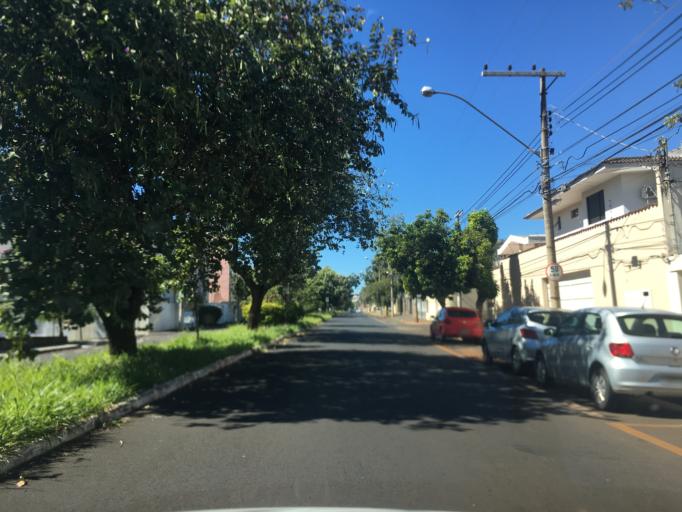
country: BR
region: Minas Gerais
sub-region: Uberlandia
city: Uberlandia
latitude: -18.9332
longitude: -48.2869
